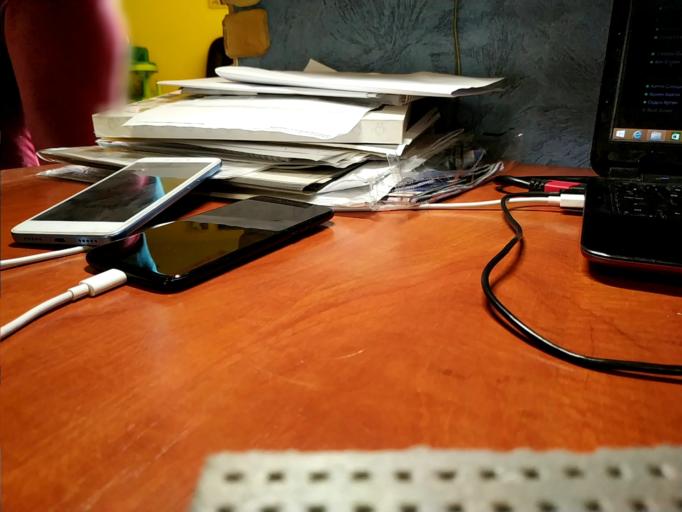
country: RU
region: Tverskaya
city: Spirovo
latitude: 57.4250
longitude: 35.0805
